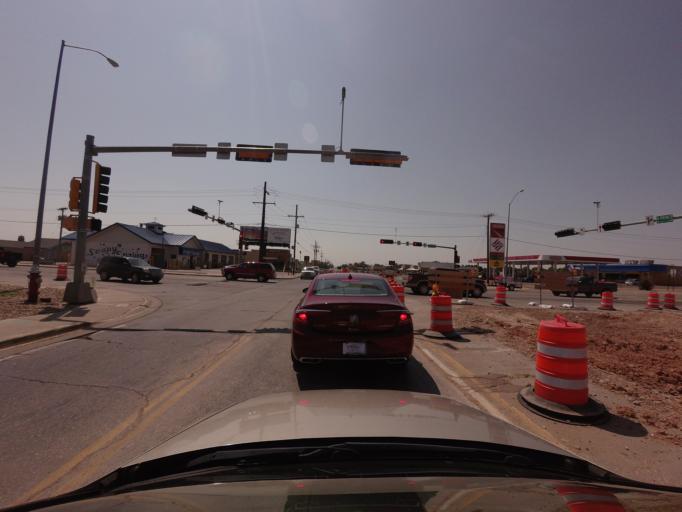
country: US
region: New Mexico
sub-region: Curry County
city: Clovis
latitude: 34.4341
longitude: -103.1964
